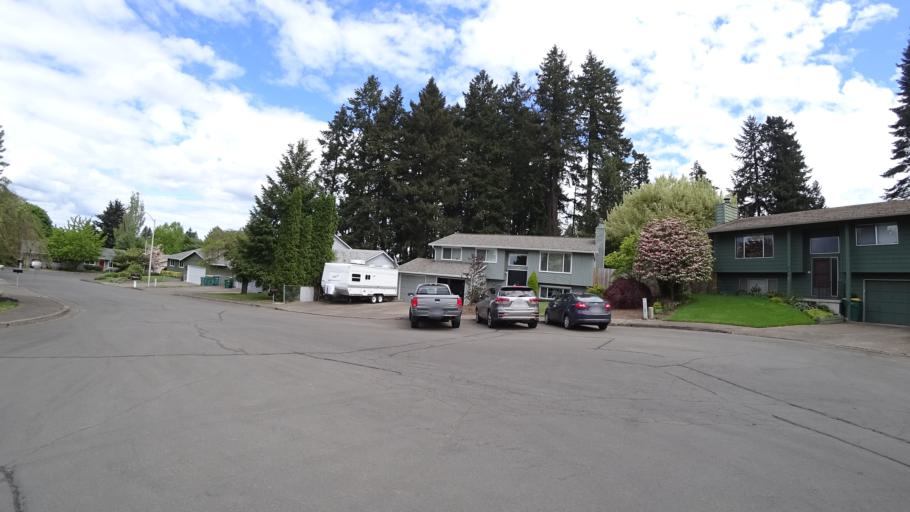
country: US
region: Oregon
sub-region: Washington County
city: Aloha
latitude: 45.4721
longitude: -122.8591
